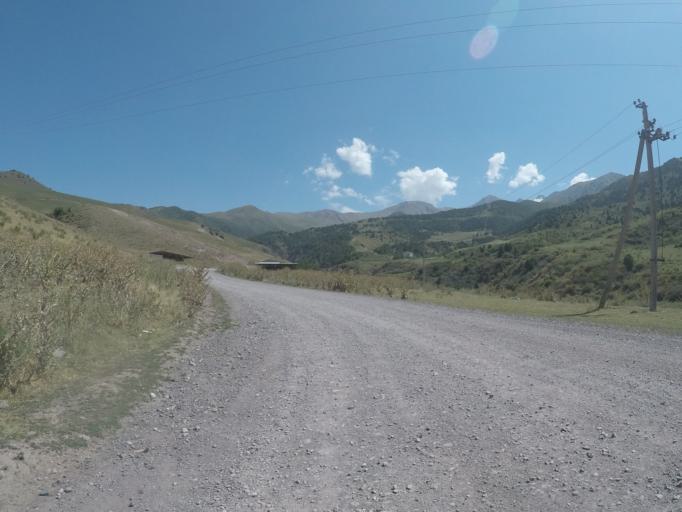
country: KG
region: Chuy
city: Bishkek
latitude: 42.6489
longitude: 74.5114
